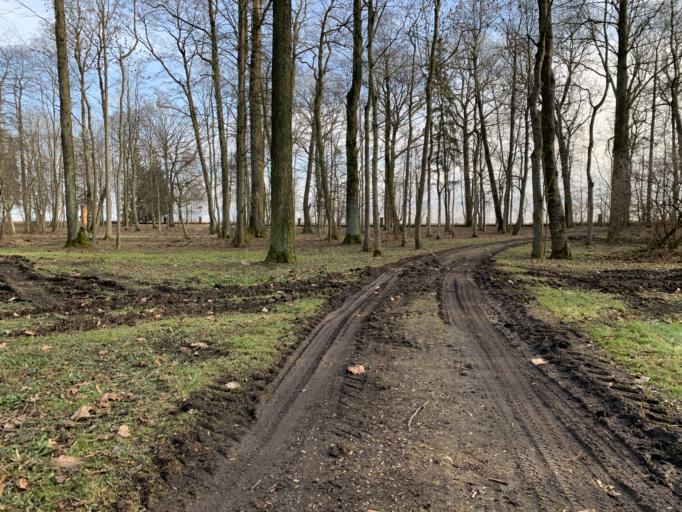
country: BY
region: Minsk
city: Nyasvizh
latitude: 53.2272
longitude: 26.7067
